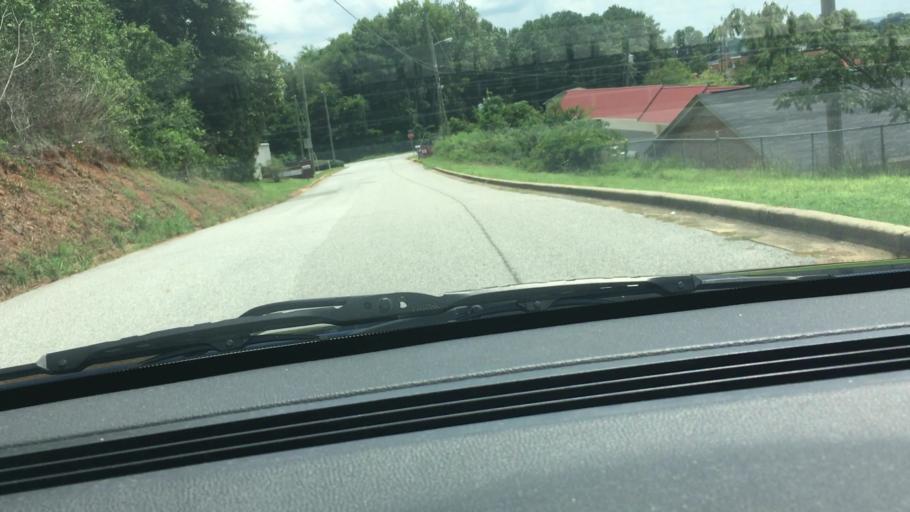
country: US
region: Alabama
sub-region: Tuscaloosa County
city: Northport
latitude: 33.2422
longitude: -87.5842
